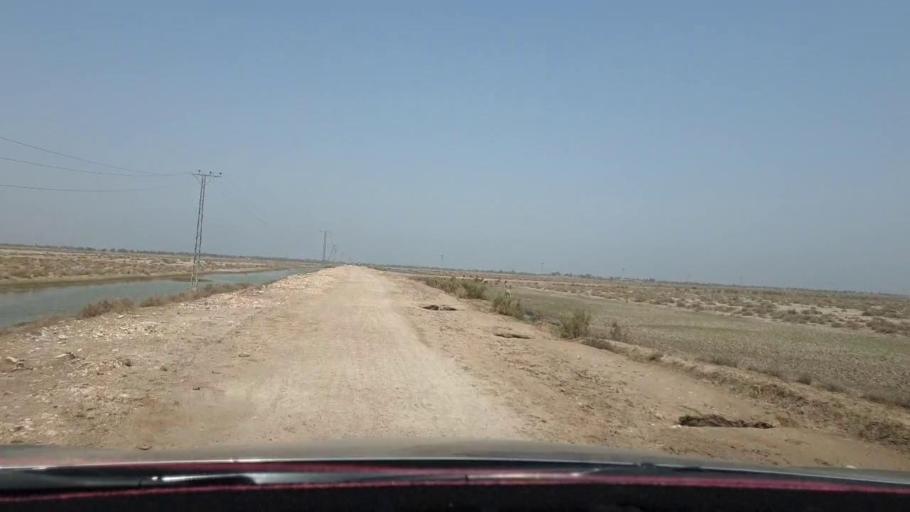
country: PK
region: Sindh
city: Warah
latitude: 27.3822
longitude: 67.6778
